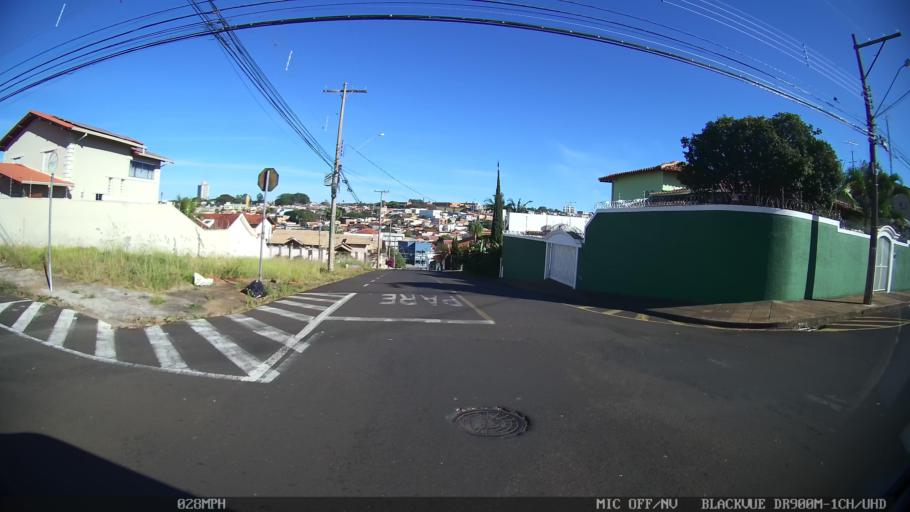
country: BR
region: Sao Paulo
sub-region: Franca
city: Franca
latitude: -20.5442
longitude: -47.4062
